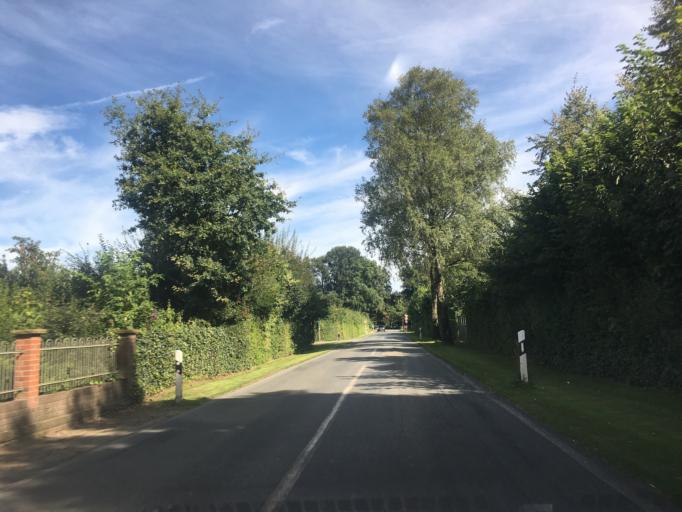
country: DE
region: North Rhine-Westphalia
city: Olfen
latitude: 51.7237
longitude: 7.3503
